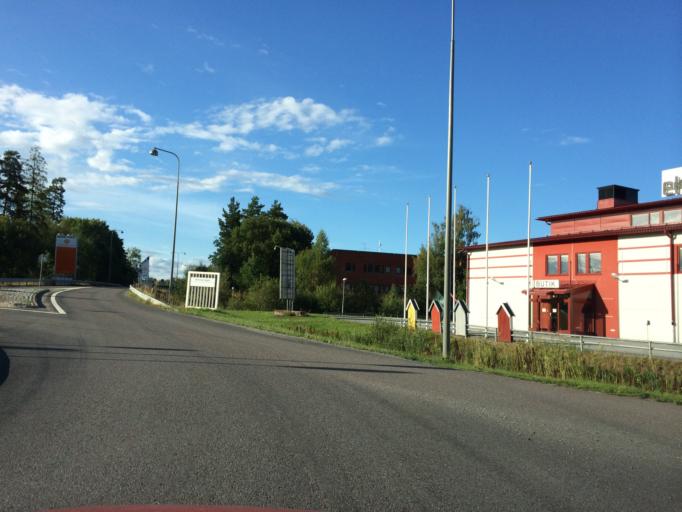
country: SE
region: Stockholm
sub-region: Huddinge Kommun
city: Segeltorp
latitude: 59.2655
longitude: 17.9266
